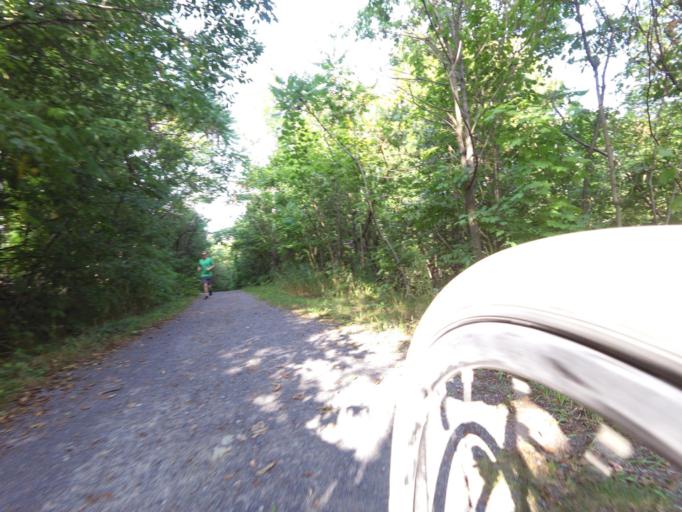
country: CA
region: Ontario
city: Kingston
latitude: 44.4250
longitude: -76.5662
